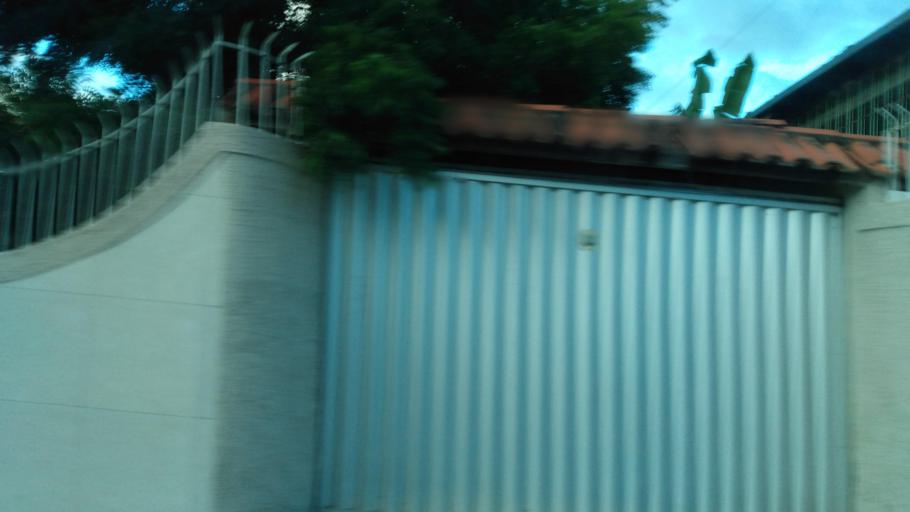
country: BR
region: Pernambuco
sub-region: Bezerros
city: Bezerros
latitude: -8.2366
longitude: -35.7509
